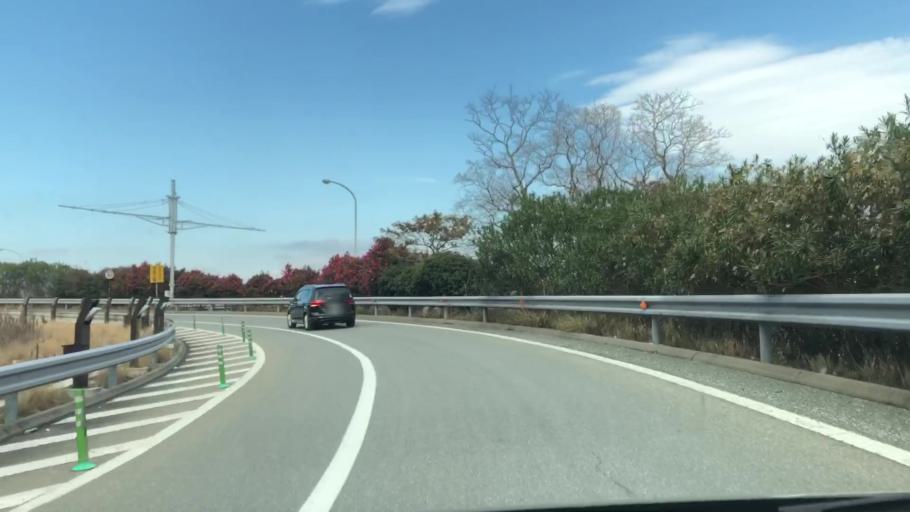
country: JP
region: Saga Prefecture
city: Tosu
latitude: 33.3975
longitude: 130.5399
